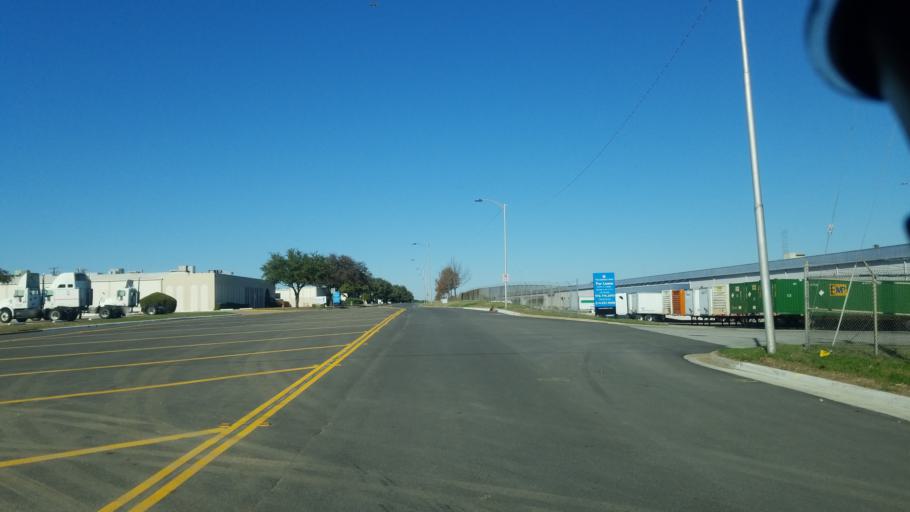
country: US
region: Texas
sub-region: Tarrant County
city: Arlington
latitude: 32.7498
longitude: -97.0542
